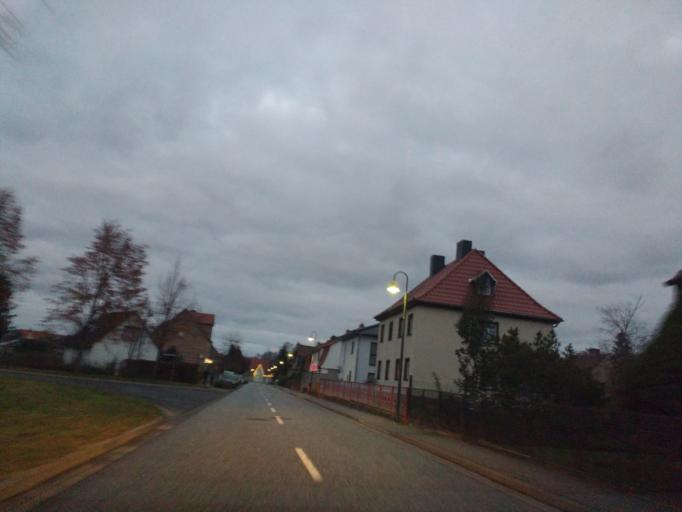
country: DE
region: Saxony-Anhalt
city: Bad Lauchstadt
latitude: 51.3833
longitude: 11.8630
